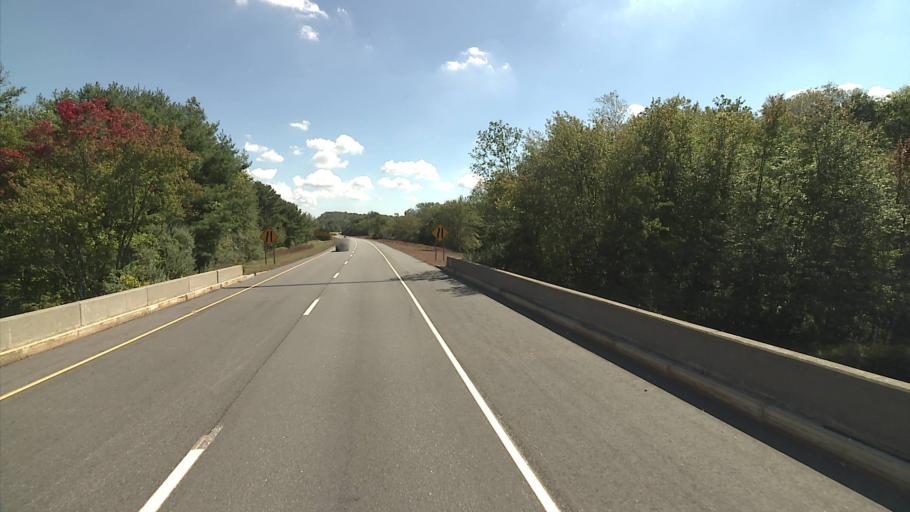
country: US
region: Connecticut
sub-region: New London County
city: Colchester
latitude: 41.4703
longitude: -72.2888
